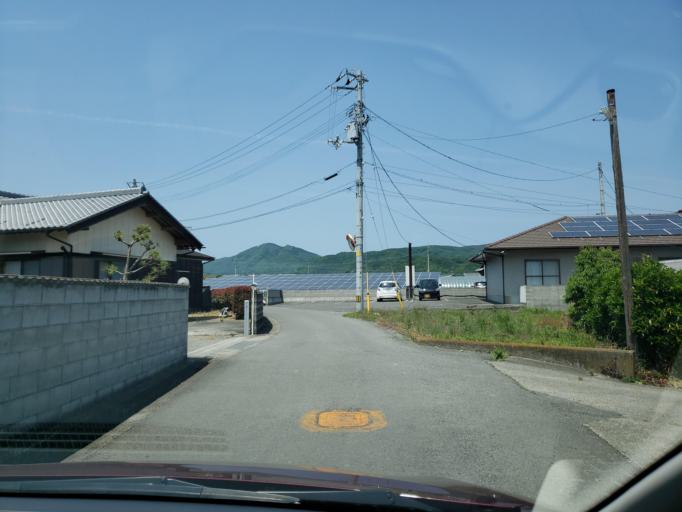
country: JP
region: Tokushima
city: Kamojimacho-jogejima
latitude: 34.0932
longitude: 134.2684
